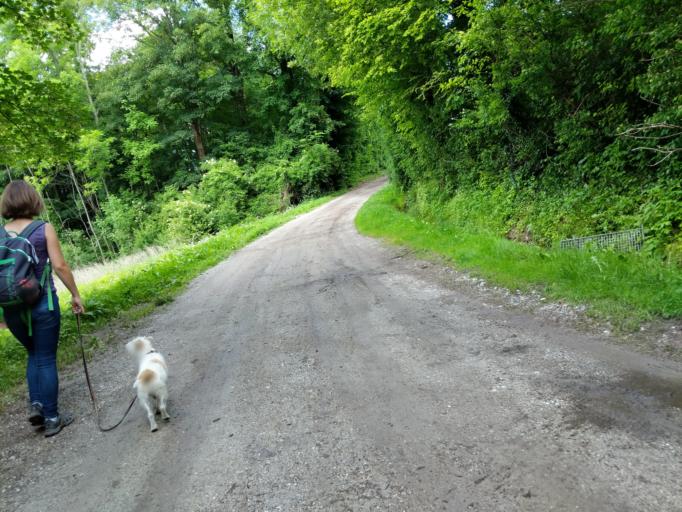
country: DE
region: Bavaria
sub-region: Upper Bavaria
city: Seefeld
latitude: 48.0167
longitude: 11.1963
